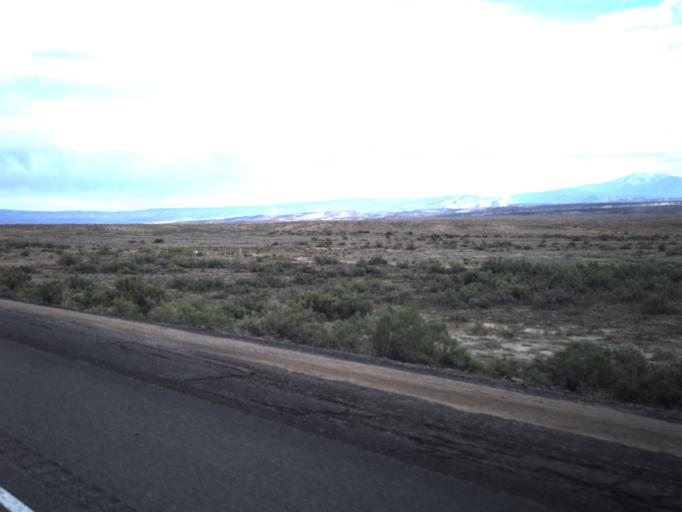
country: US
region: Utah
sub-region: Grand County
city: Moab
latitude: 38.9371
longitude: -109.4854
